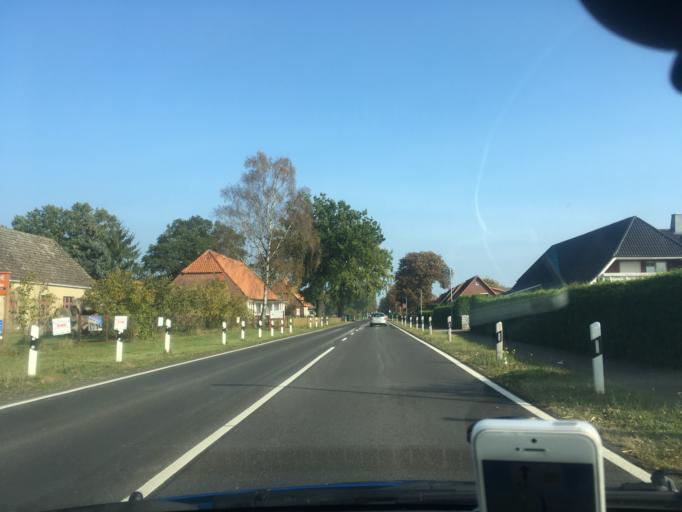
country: DE
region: Mecklenburg-Vorpommern
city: Stralendorf
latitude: 53.4881
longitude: 11.2746
